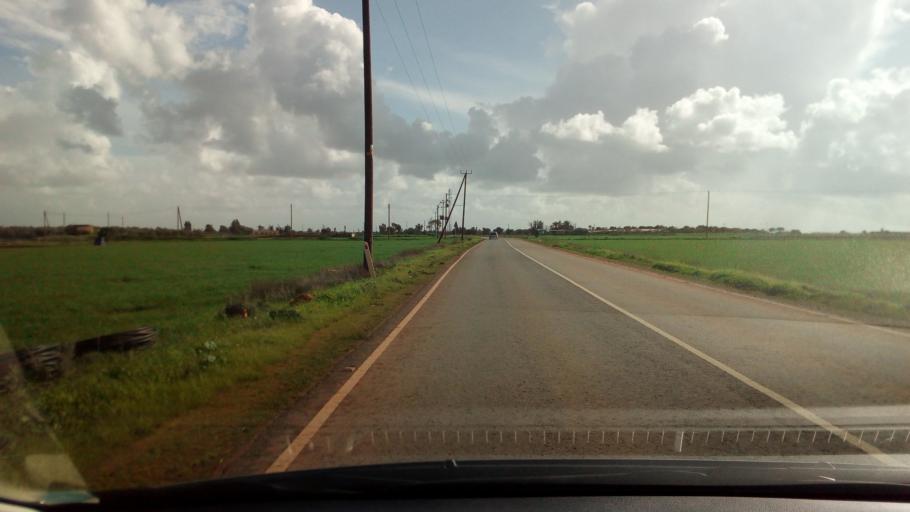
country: CY
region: Ammochostos
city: Achna
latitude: 35.0590
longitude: 33.8054
